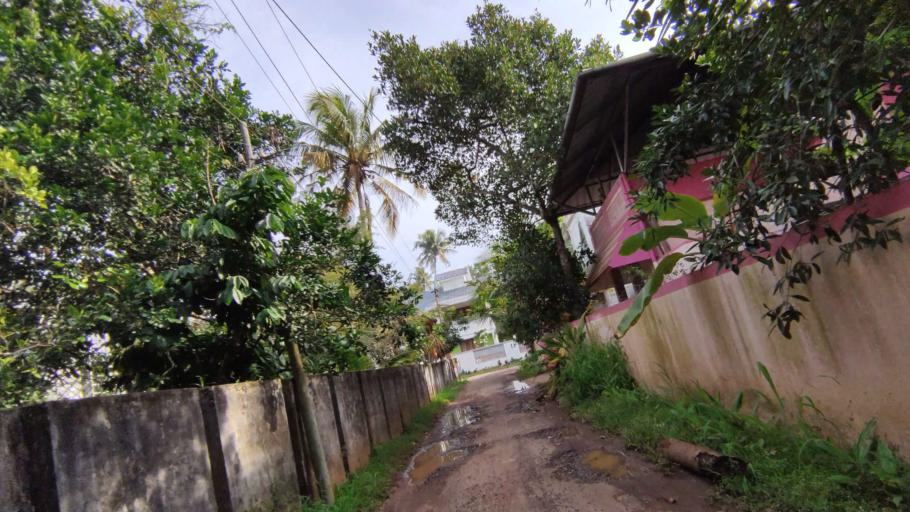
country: IN
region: Kerala
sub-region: Alappuzha
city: Shertallai
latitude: 9.6290
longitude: 76.3342
